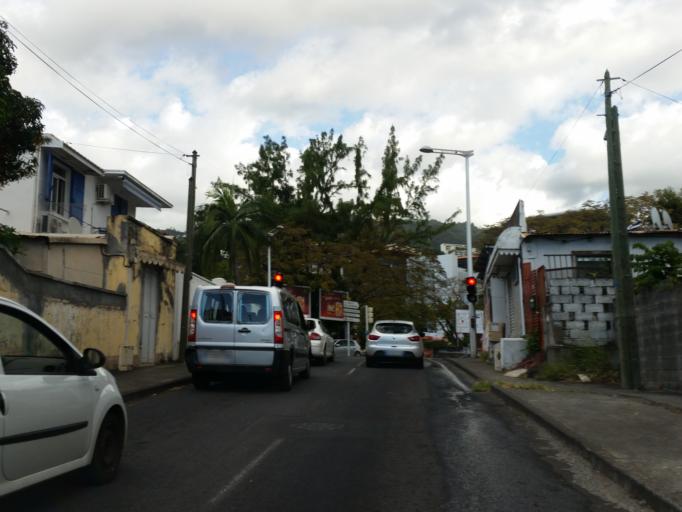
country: RE
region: Reunion
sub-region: Reunion
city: Saint-Denis
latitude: -20.8890
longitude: 55.4453
